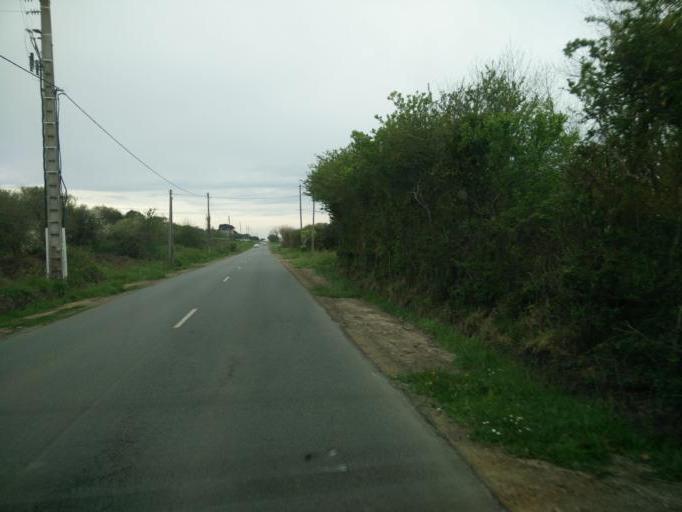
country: FR
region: Brittany
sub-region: Departement des Cotes-d'Armor
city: Trebeurden
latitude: 48.7902
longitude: -3.5664
